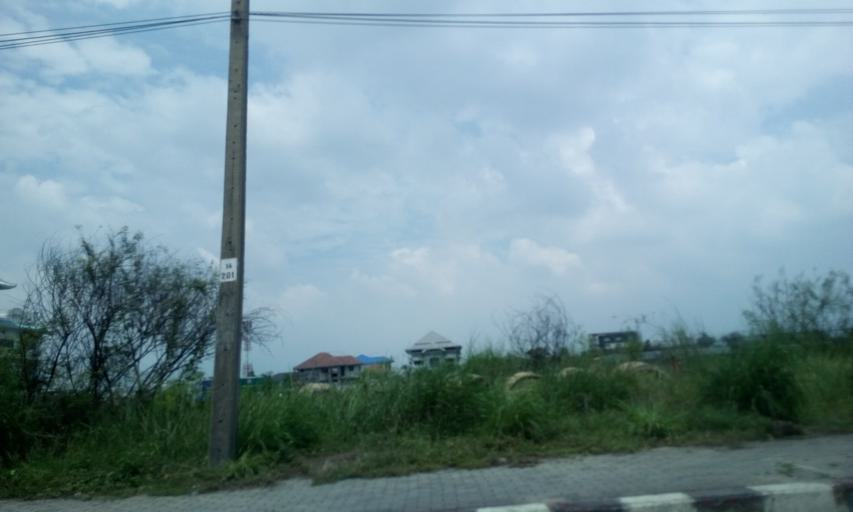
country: TH
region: Bangkok
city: Don Mueang
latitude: 13.9374
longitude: 100.5566
